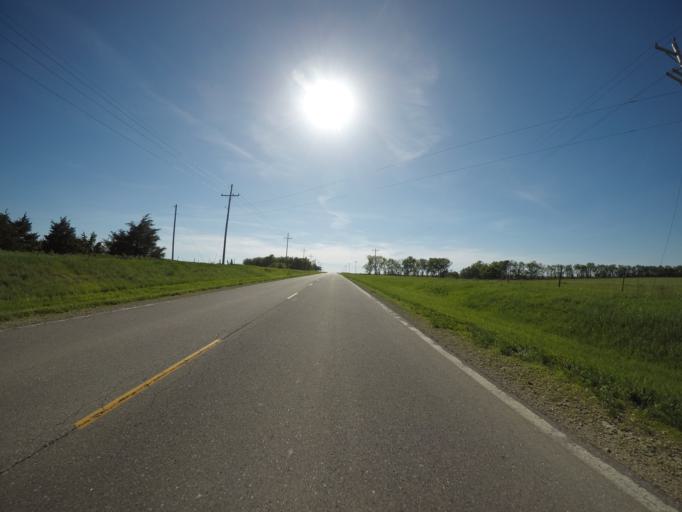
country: US
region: Kansas
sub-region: Clay County
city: Clay Center
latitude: 39.3646
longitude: -96.8756
